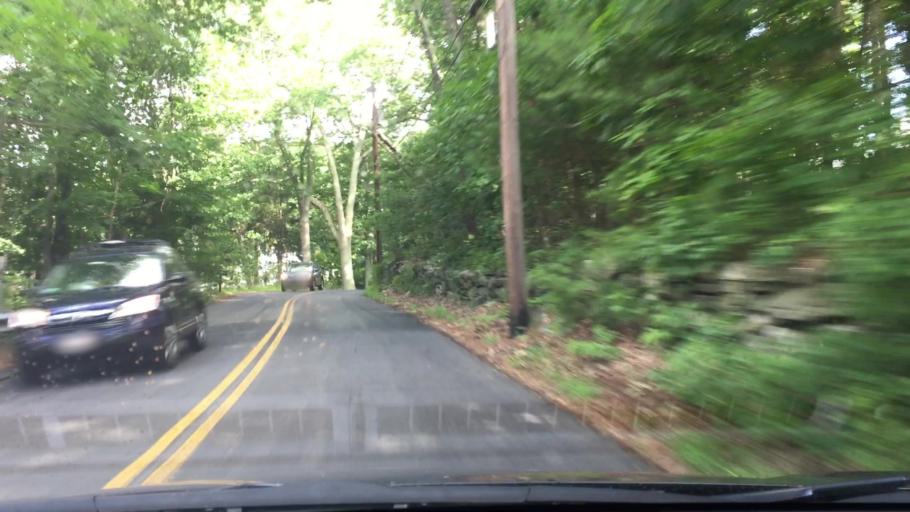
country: US
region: Massachusetts
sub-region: Middlesex County
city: Acton
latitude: 42.4934
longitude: -71.4356
